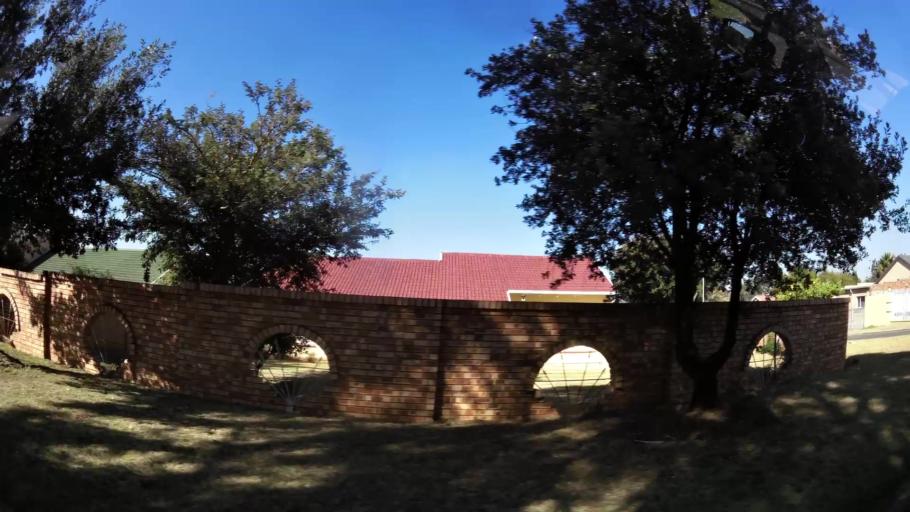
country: ZA
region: Gauteng
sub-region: City of Johannesburg Metropolitan Municipality
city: Roodepoort
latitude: -26.1481
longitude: 27.8365
